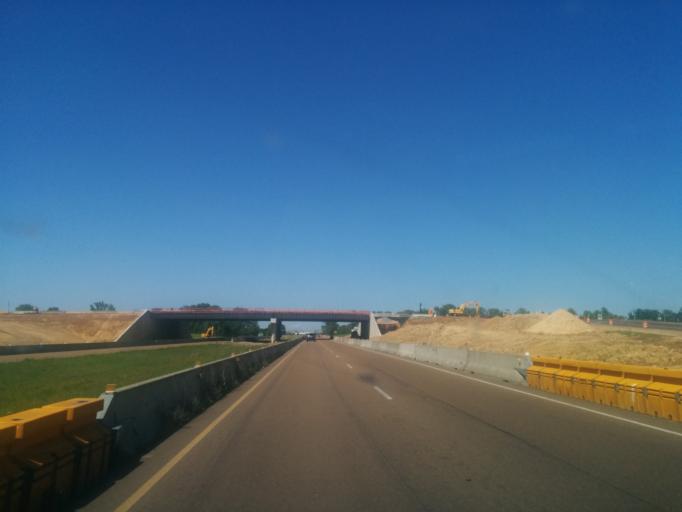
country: US
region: Mississippi
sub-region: Madison County
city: Madison
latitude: 32.5158
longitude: -90.1023
